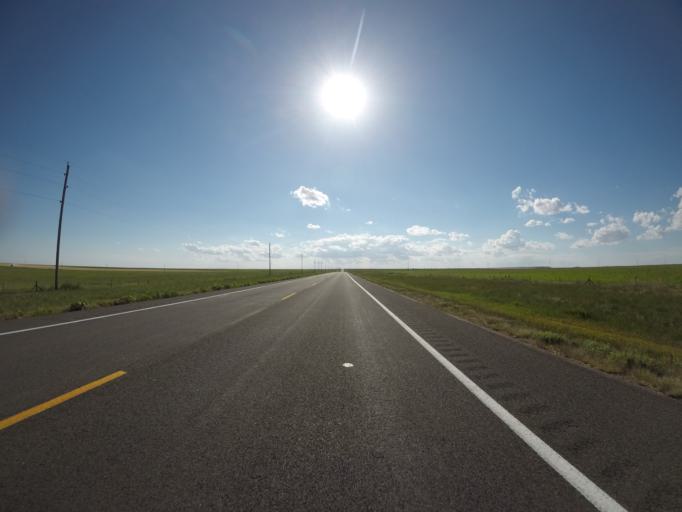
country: US
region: Colorado
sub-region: Morgan County
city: Fort Morgan
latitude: 40.6106
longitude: -103.7477
